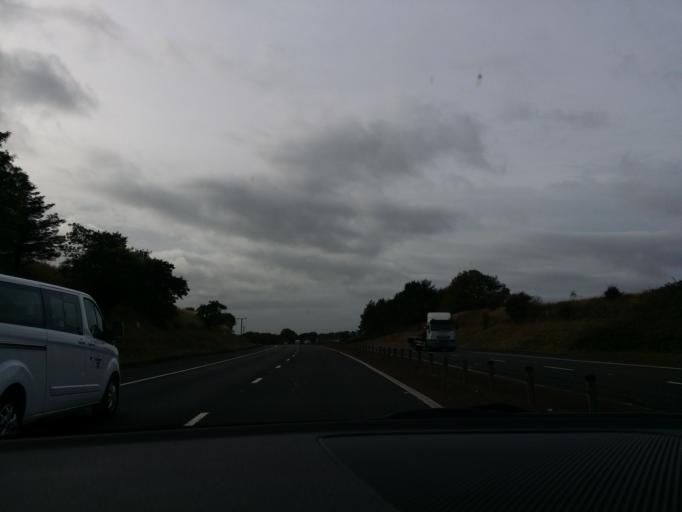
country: GB
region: Scotland
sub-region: West Lothian
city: Linlithgow
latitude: 55.9887
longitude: -3.5744
